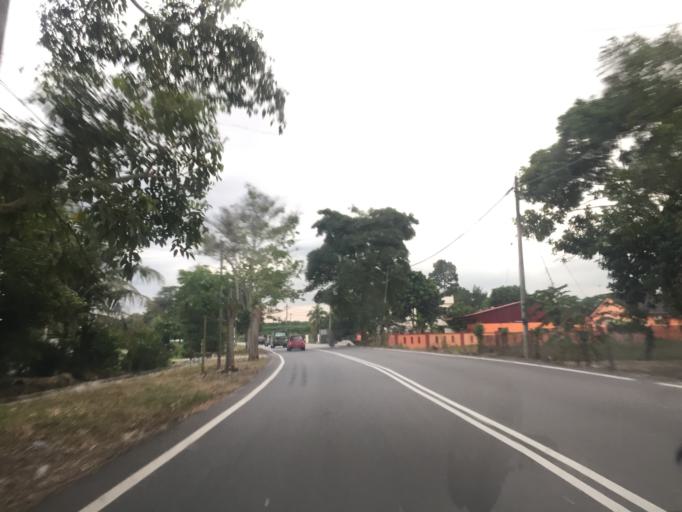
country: MY
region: Penang
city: Tasek Glugor
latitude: 5.5387
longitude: 100.5092
